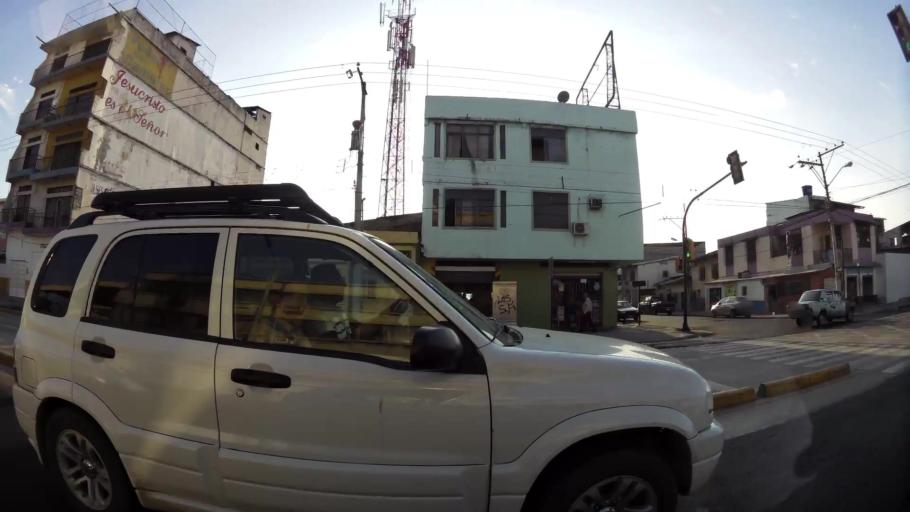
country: EC
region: Guayas
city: Guayaquil
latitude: -2.2163
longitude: -79.8976
